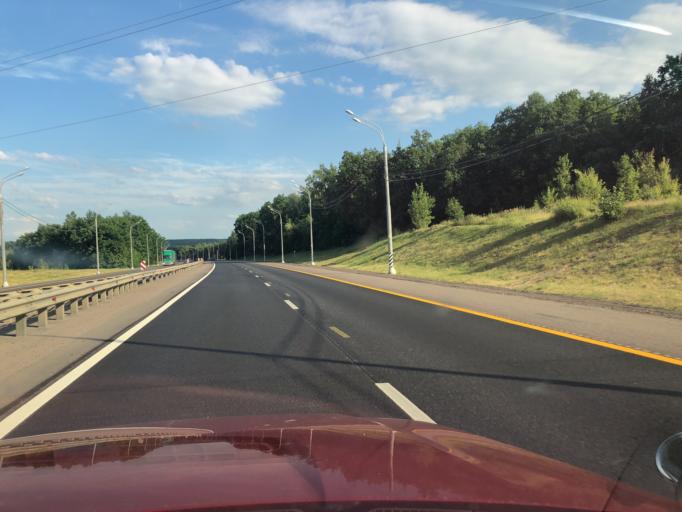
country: RU
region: Lipetsk
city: Zadonsk
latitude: 52.3859
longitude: 38.8688
